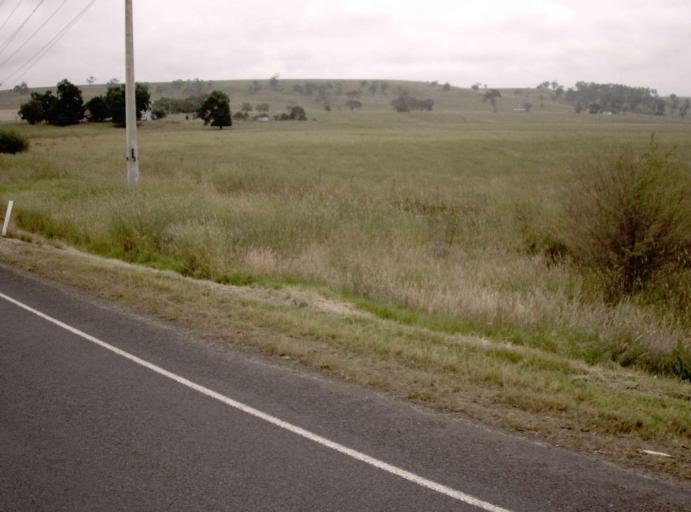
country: AU
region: Victoria
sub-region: Latrobe
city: Traralgon
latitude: -38.2503
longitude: 146.5403
